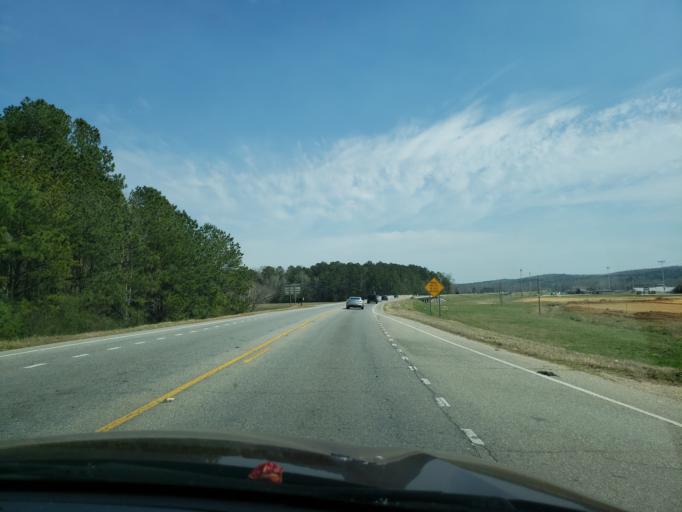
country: US
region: Alabama
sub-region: Elmore County
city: Wetumpka
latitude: 32.5540
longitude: -86.2134
